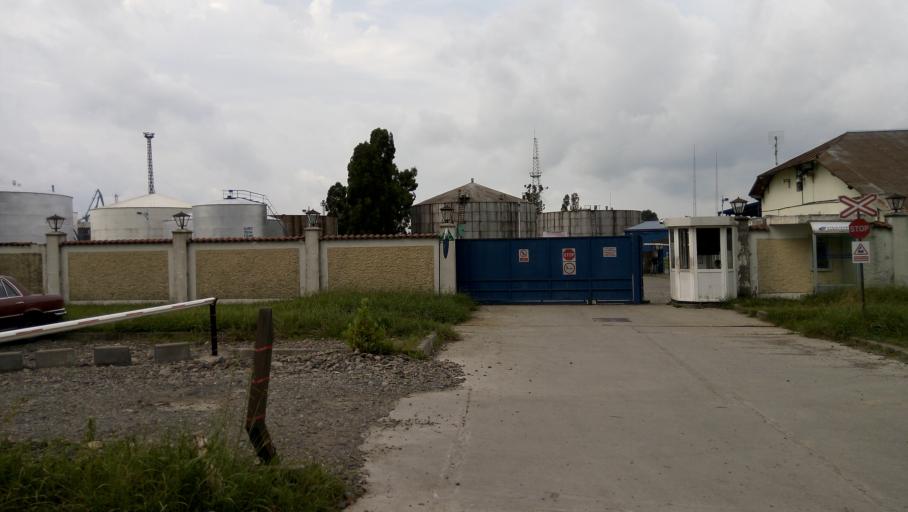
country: GE
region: Ajaria
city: Batumi
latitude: 41.6425
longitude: 41.6588
